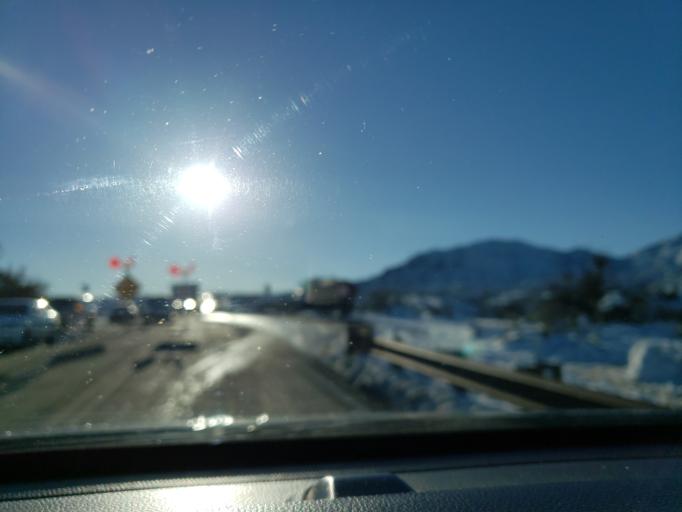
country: US
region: Arizona
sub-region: Maricopa County
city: Carefree
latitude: 33.8769
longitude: -111.8175
